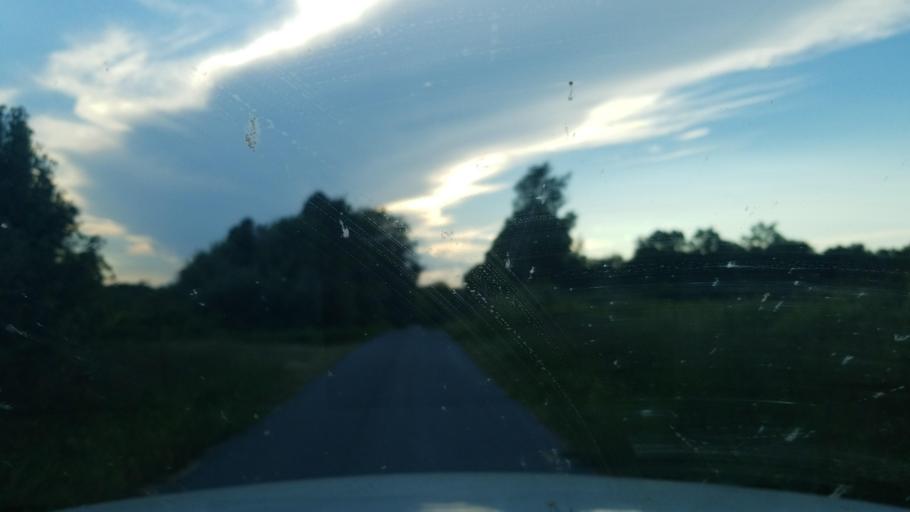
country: US
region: Illinois
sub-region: Saline County
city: Carrier Mills
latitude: 37.7903
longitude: -88.7004
